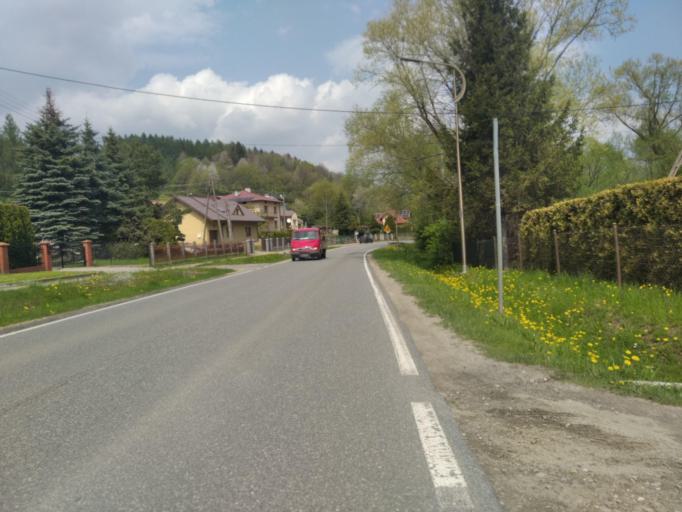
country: PL
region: Subcarpathian Voivodeship
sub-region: Powiat krosnienski
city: Rymanow
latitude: 49.5607
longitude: 21.8572
